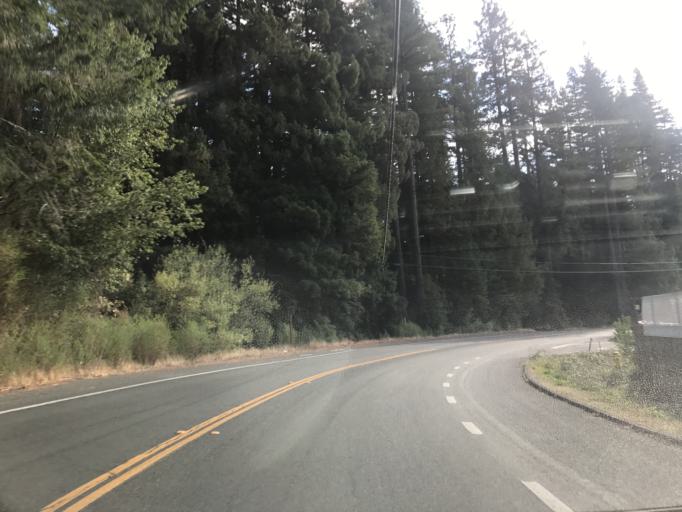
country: US
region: California
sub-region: Sonoma County
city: Guerneville
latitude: 38.5186
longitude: -122.9964
